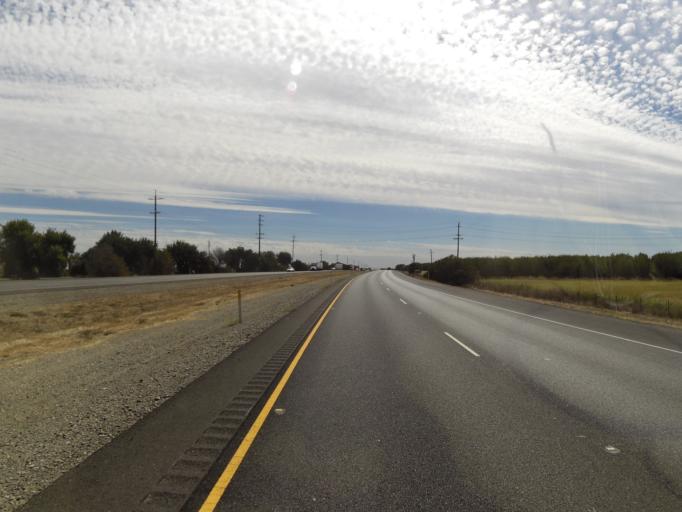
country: US
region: California
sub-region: Colusa County
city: Williams
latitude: 39.1245
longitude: -122.1283
